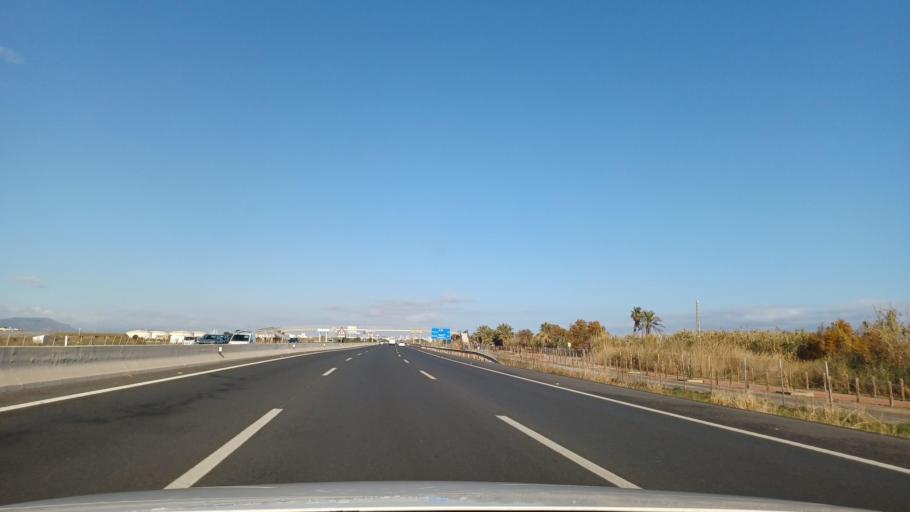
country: ES
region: Valencia
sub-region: Provincia de Valencia
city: Meliana
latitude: 39.5200
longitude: -0.3188
